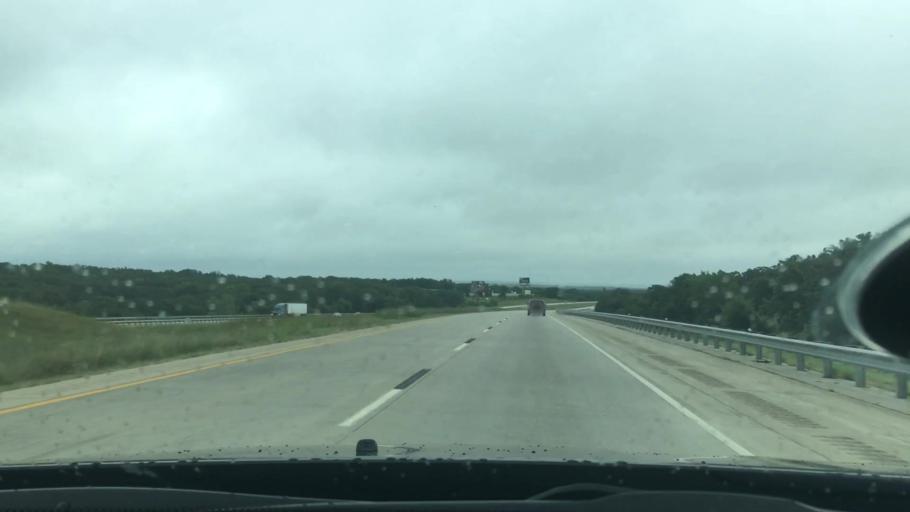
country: US
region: Oklahoma
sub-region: Okfuskee County
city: Boley
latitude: 35.3843
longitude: -96.5068
